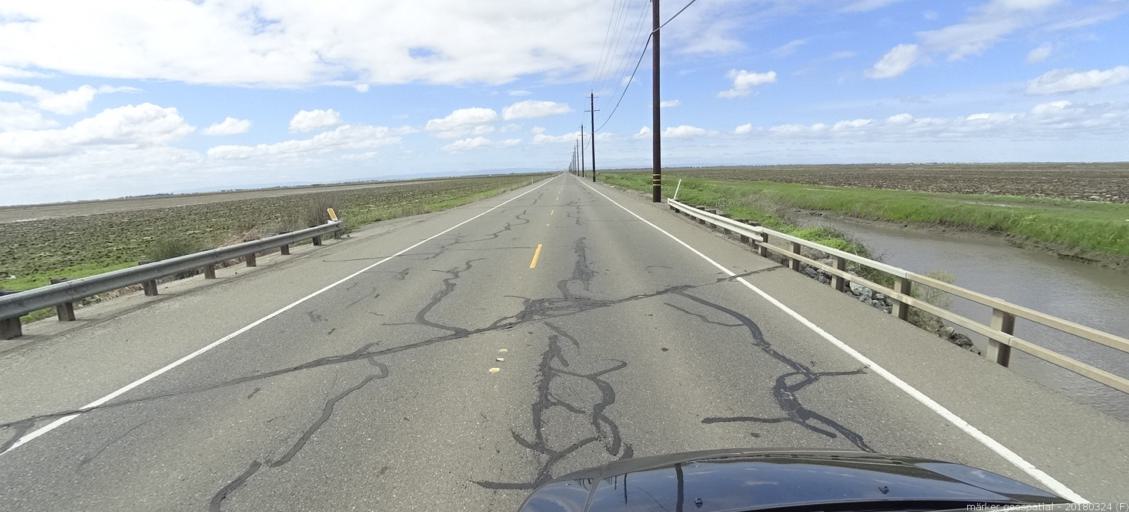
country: US
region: California
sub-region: Sacramento County
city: Elverta
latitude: 38.7143
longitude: -121.5121
